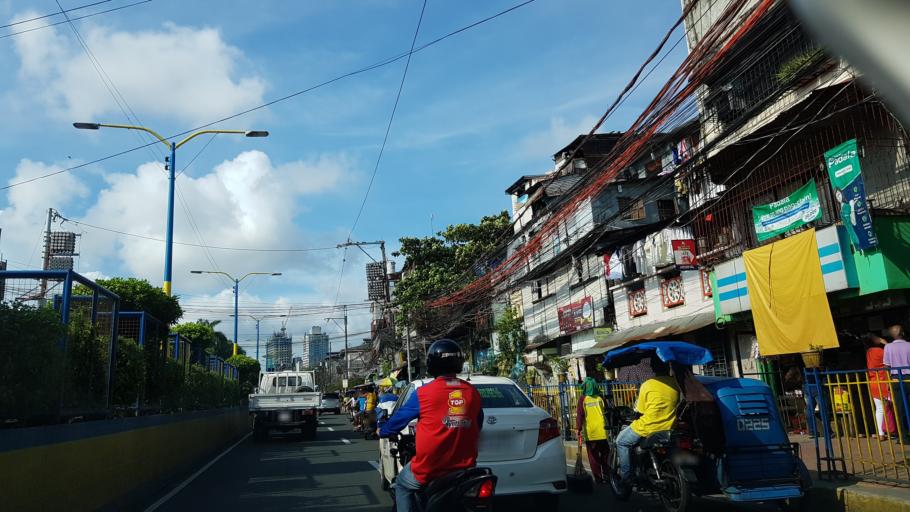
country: PH
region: Metro Manila
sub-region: Mandaluyong
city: Mandaluyong City
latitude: 14.5815
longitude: 121.0367
